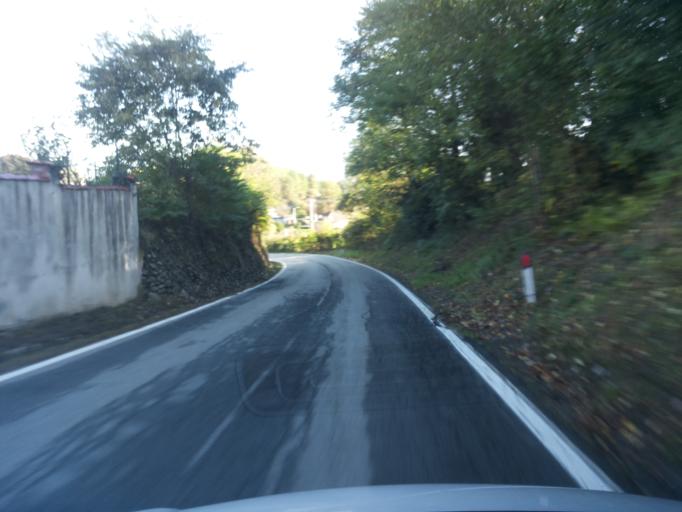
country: IT
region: Piedmont
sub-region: Provincia di Torino
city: Vische
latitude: 45.3298
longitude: 7.9511
